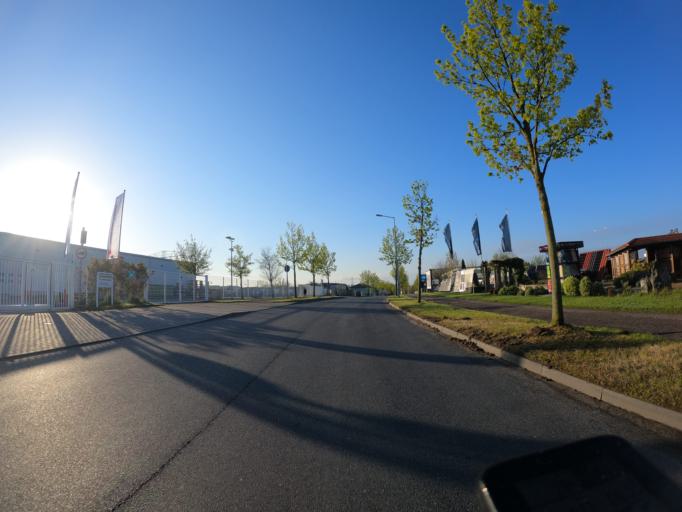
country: DE
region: Brandenburg
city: Neuenhagen
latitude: 52.5355
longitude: 13.7100
